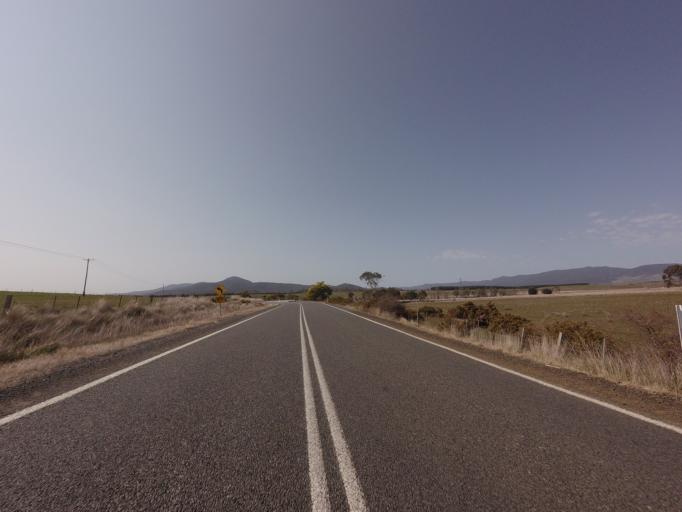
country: AU
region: Tasmania
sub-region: Northern Midlands
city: Evandale
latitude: -41.7993
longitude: 147.6990
